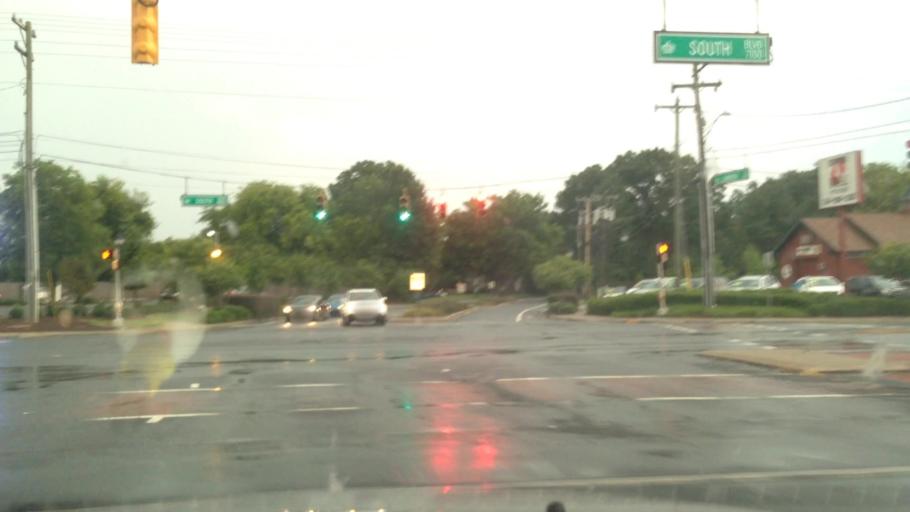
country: US
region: North Carolina
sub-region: Mecklenburg County
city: Pineville
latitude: 35.1377
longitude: -80.8767
